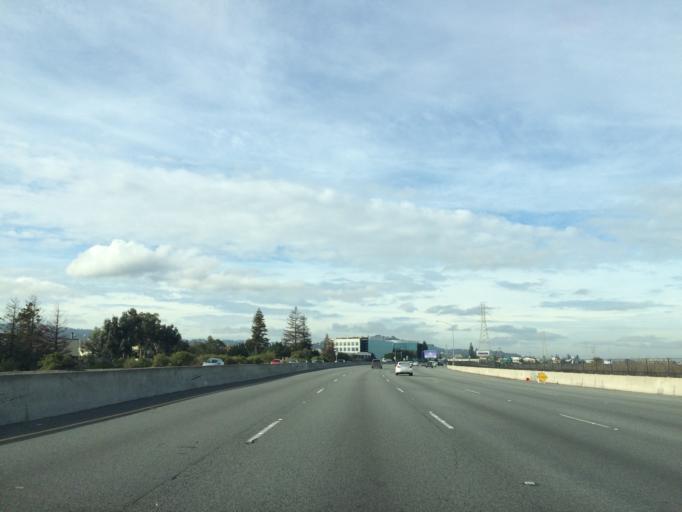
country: US
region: California
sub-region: San Mateo County
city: Redwood City
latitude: 37.4967
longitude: -122.2341
